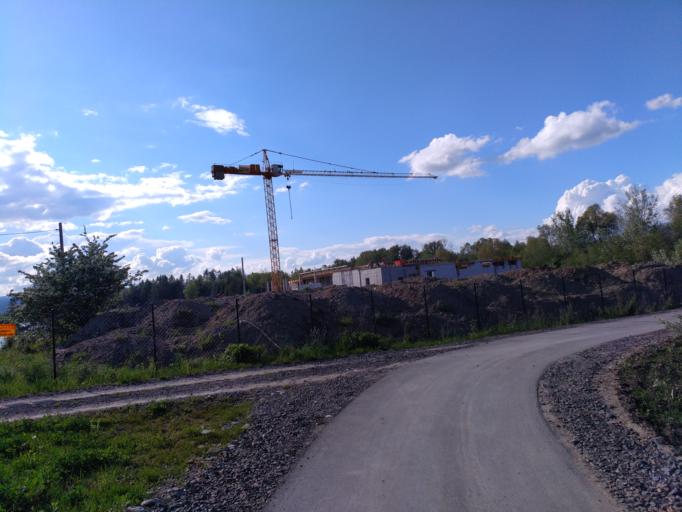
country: PL
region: Lesser Poland Voivodeship
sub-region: Powiat nowosadecki
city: Stary Sacz
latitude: 49.5810
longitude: 20.6457
